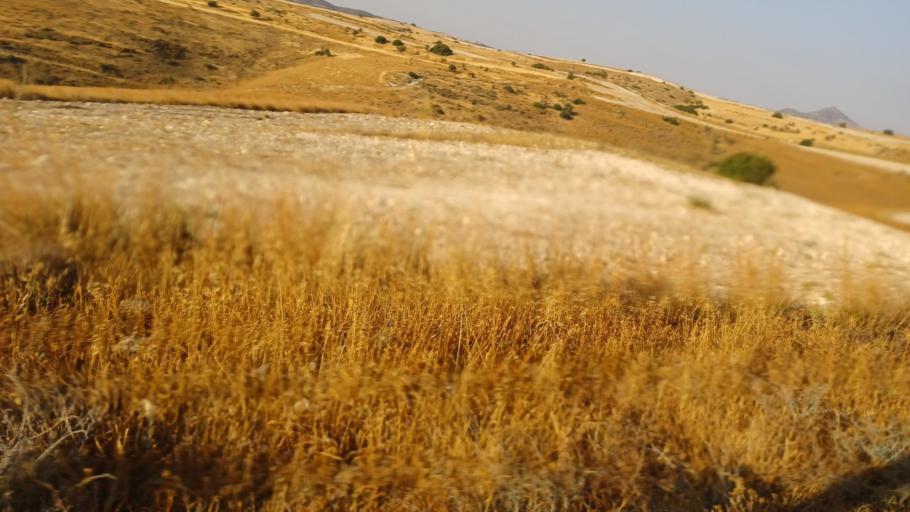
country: CY
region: Larnaka
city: Psevdas
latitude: 34.9211
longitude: 33.4894
